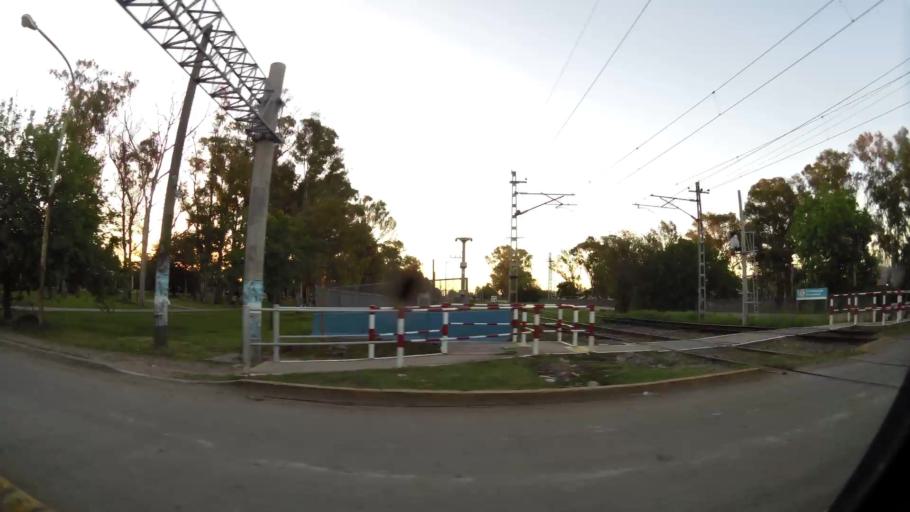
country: AR
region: Buenos Aires
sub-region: Partido de Almirante Brown
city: Adrogue
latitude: -34.8021
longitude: -58.3342
